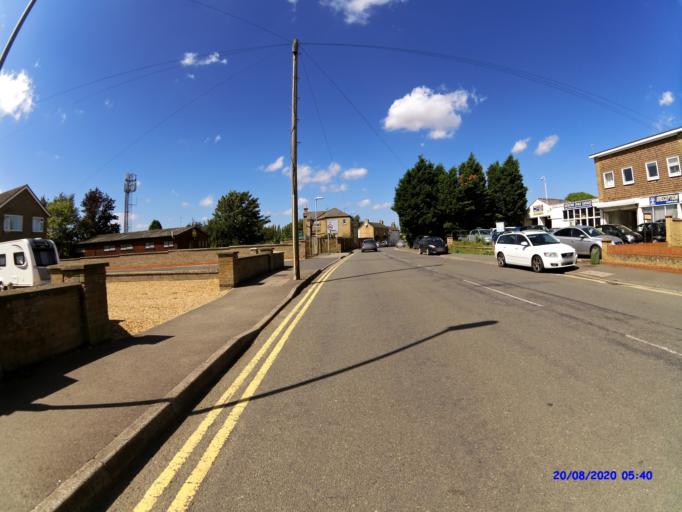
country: GB
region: England
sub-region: Cambridgeshire
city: Whittlesey
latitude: 52.5528
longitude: -0.1248
